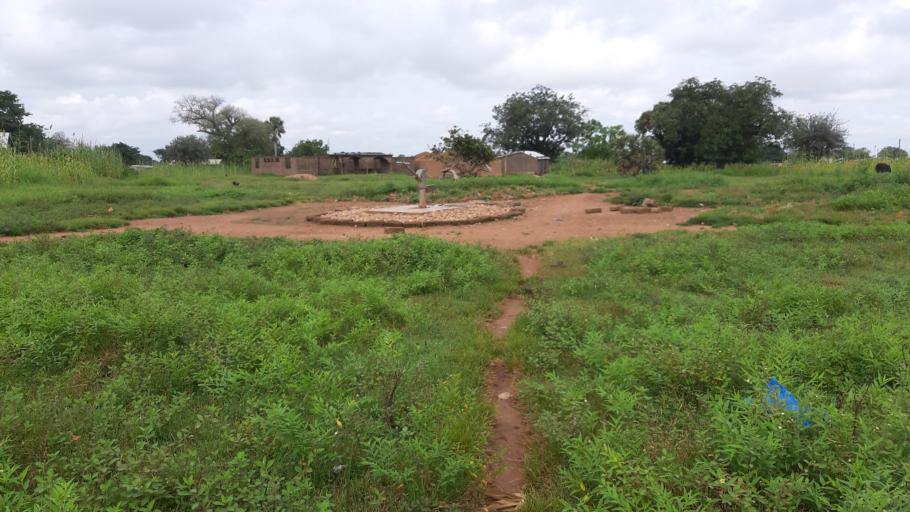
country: GH
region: Upper East
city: Bolgatanga
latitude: 10.7834
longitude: -0.7845
